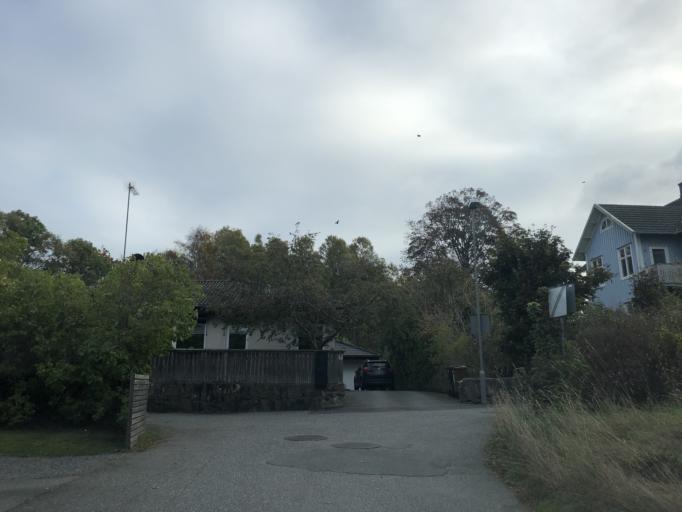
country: SE
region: Vaestra Goetaland
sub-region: Goteborg
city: Majorna
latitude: 57.6806
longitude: 11.8842
